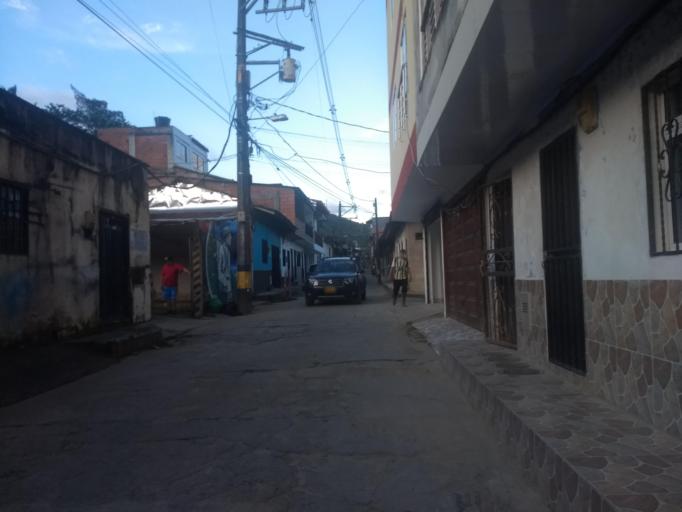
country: CO
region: Antioquia
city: San Carlos
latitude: 6.1891
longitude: -74.9944
